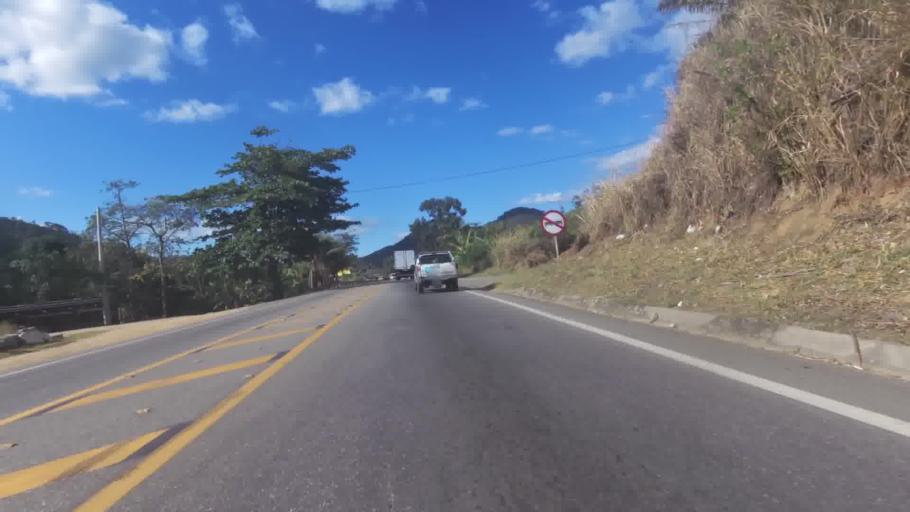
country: BR
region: Espirito Santo
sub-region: Rio Novo Do Sul
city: Rio Novo do Sul
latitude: -20.8679
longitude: -40.9396
